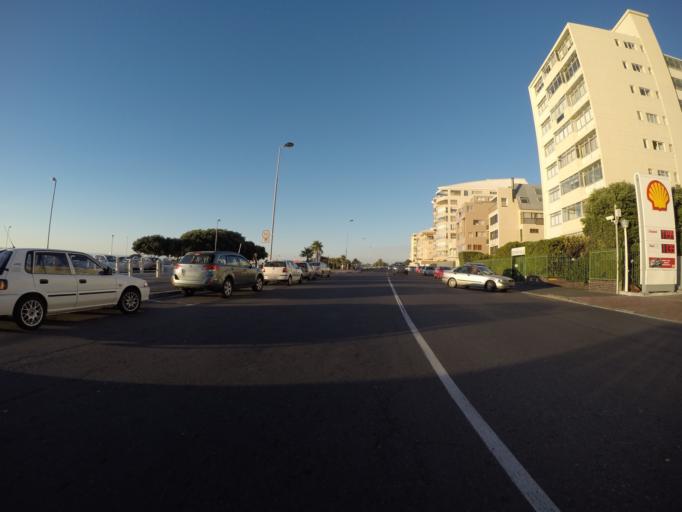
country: ZA
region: Western Cape
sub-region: City of Cape Town
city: Cape Town
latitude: -33.9055
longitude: 18.3982
